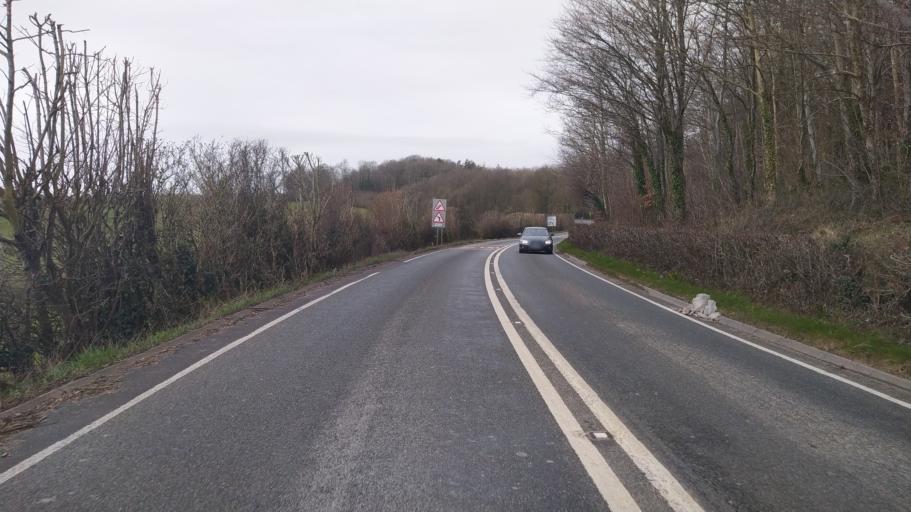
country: GB
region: England
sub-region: Somerset
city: Crewkerne
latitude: 50.8858
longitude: -2.8443
